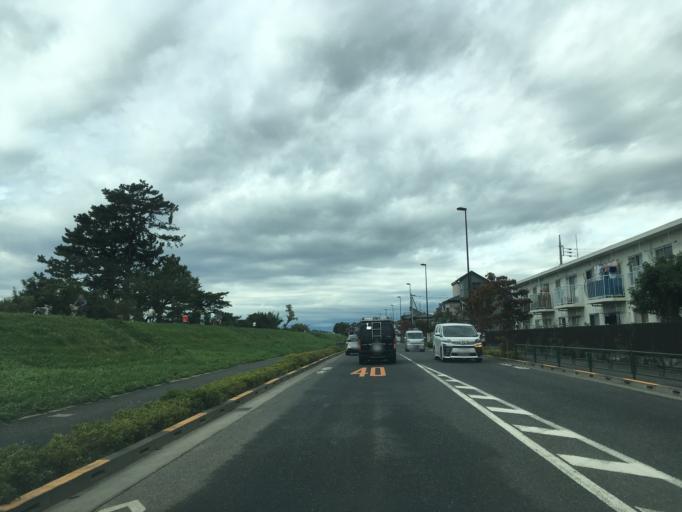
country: JP
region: Tokyo
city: Chofugaoka
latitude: 35.6364
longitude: 139.5597
